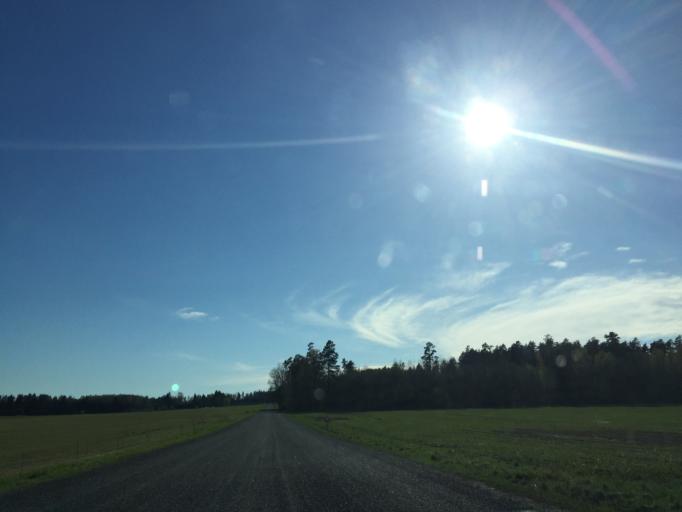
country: EE
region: Valgamaa
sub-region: Valga linn
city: Valga
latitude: 57.8297
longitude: 26.2226
